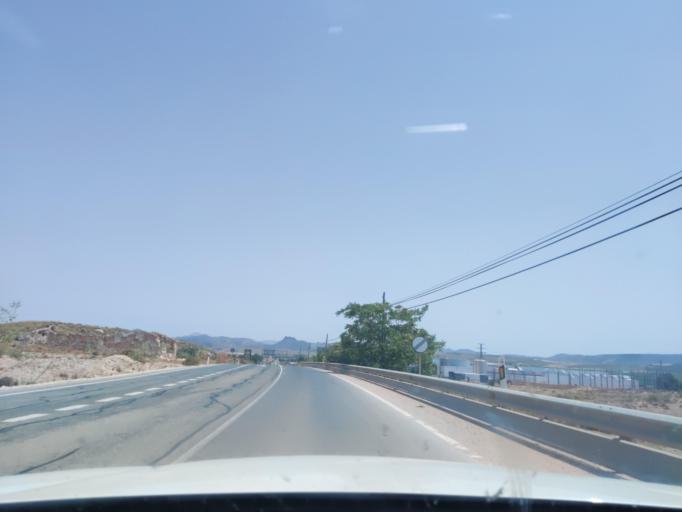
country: ES
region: Castille-La Mancha
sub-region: Provincia de Albacete
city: Hellin
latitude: 38.4996
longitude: -1.6700
